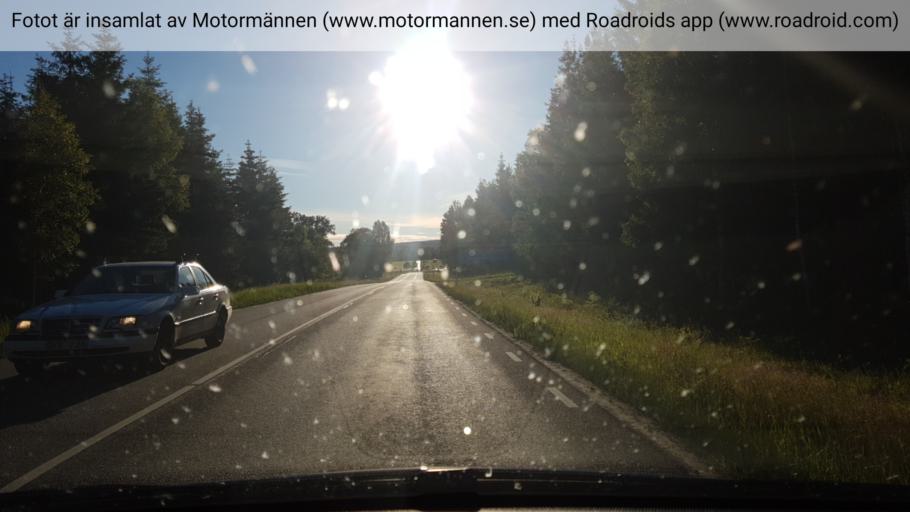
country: SE
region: Vaestra Goetaland
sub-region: Tidaholms Kommun
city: Tidaholm
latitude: 58.1921
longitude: 13.9009
